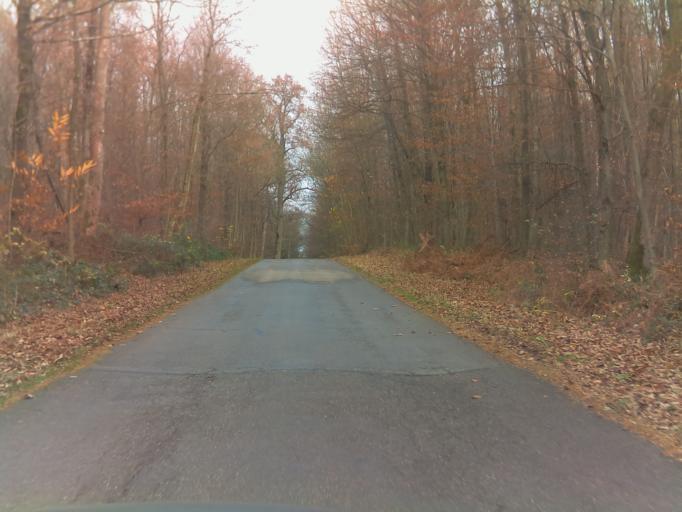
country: DE
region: Baden-Wuerttemberg
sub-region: Karlsruhe Region
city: Neunkirchen
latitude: 49.4026
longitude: 9.0153
